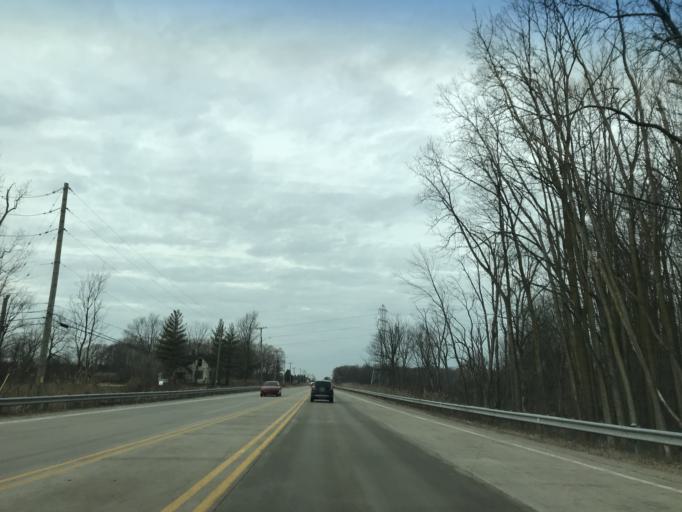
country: US
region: Michigan
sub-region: Macomb County
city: Mount Clemens
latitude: 42.6734
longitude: -82.8828
